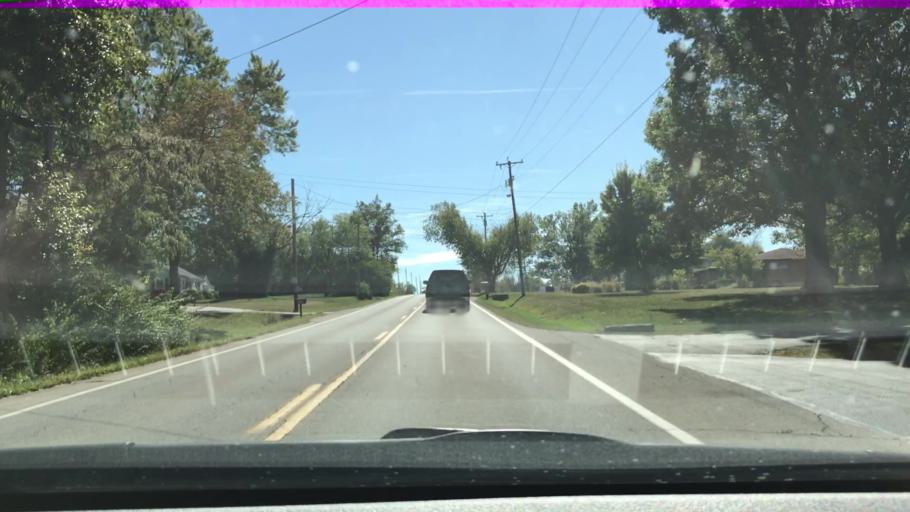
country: US
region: Ohio
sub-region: Butler County
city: Hamilton
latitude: 39.4510
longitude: -84.6211
